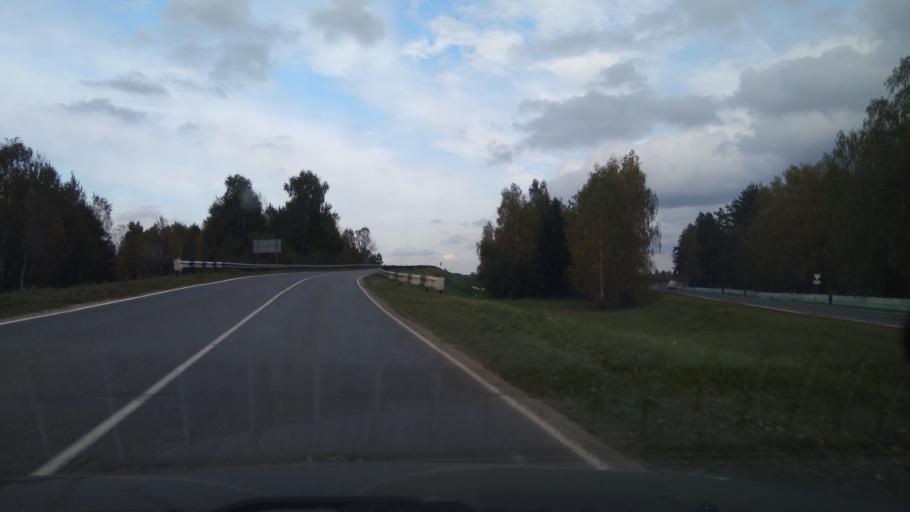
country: BY
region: Minsk
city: Dukora
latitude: 53.6574
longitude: 27.9457
